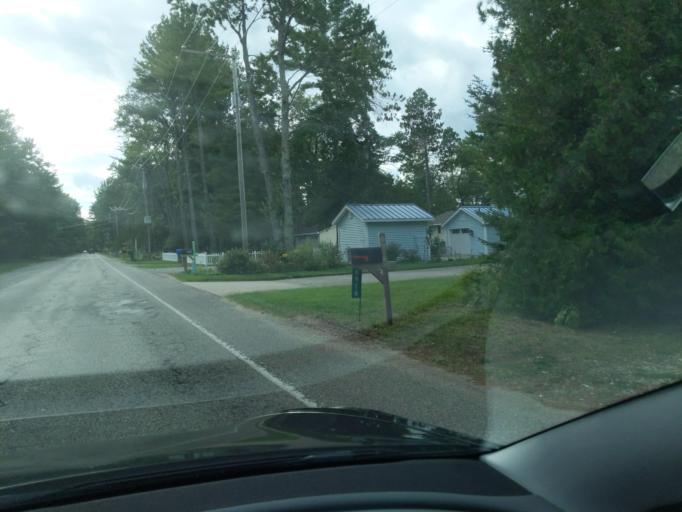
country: US
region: Michigan
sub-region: Kalkaska County
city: Rapid City
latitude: 44.8532
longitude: -85.3114
